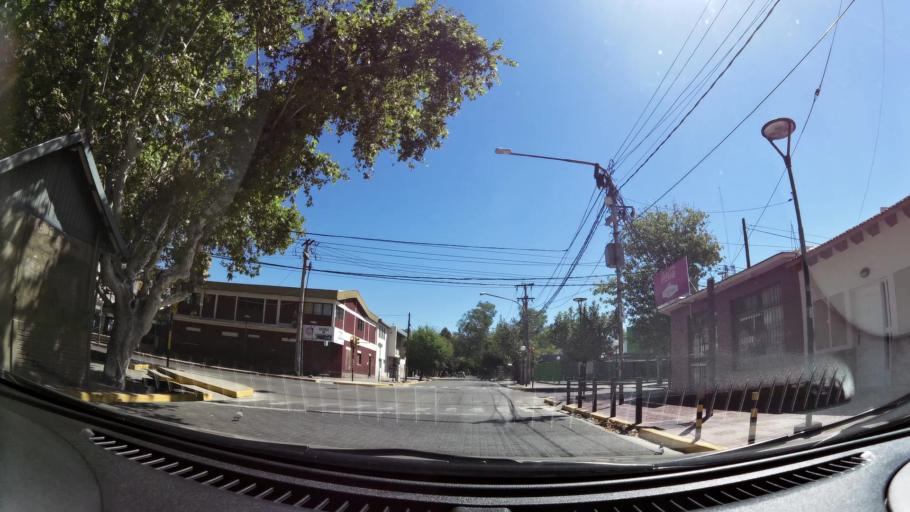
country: AR
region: Mendoza
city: Las Heras
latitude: -32.8498
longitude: -68.8411
